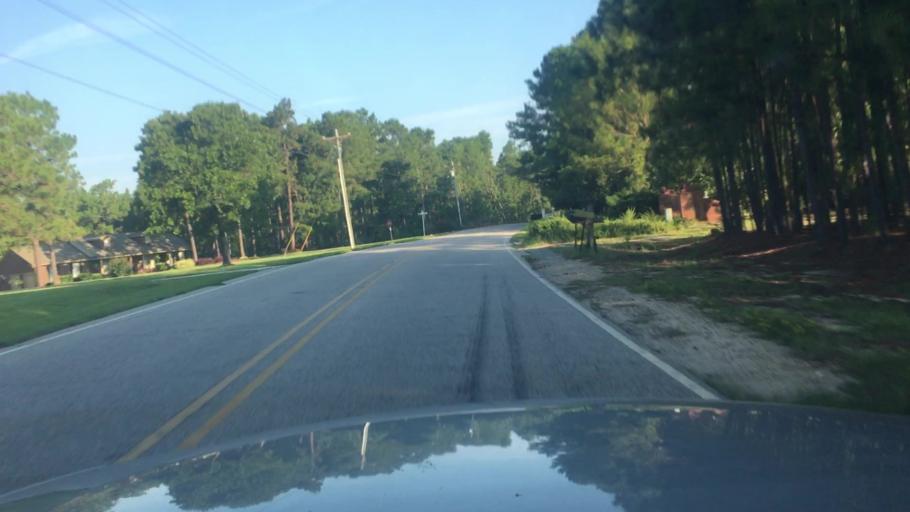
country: US
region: North Carolina
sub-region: Harnett County
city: Walkertown
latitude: 35.2119
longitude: -78.8632
